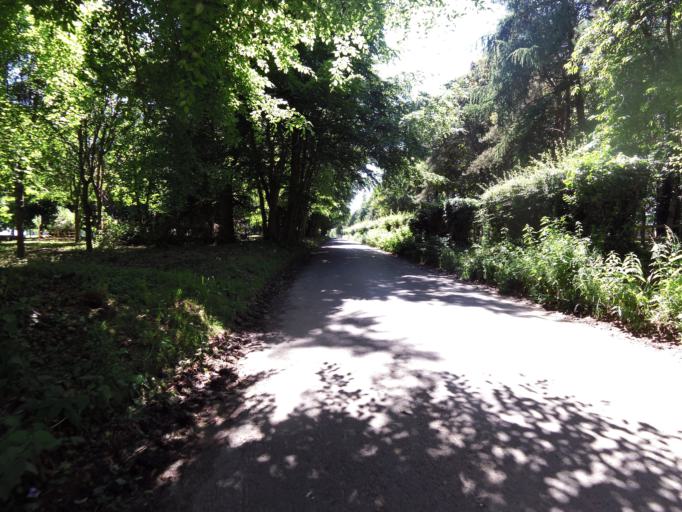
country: GB
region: England
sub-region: Suffolk
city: Felixstowe
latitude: 52.0518
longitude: 1.4494
